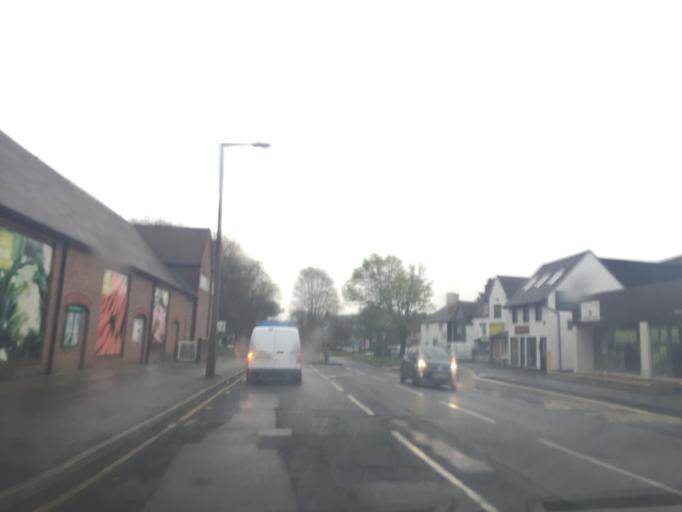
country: GB
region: England
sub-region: Essex
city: Epping
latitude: 51.6968
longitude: 0.1080
